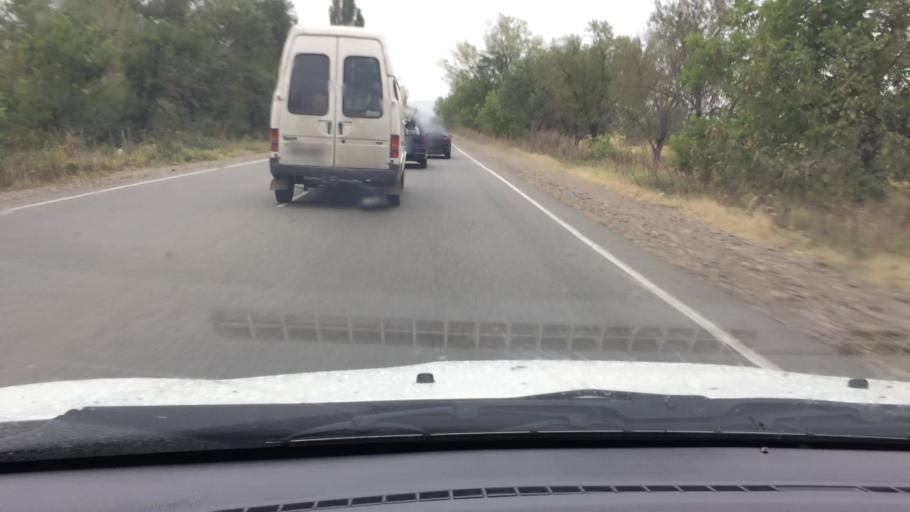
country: GE
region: Kvemo Kartli
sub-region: Marneuli
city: Marneuli
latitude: 41.5519
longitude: 44.7763
